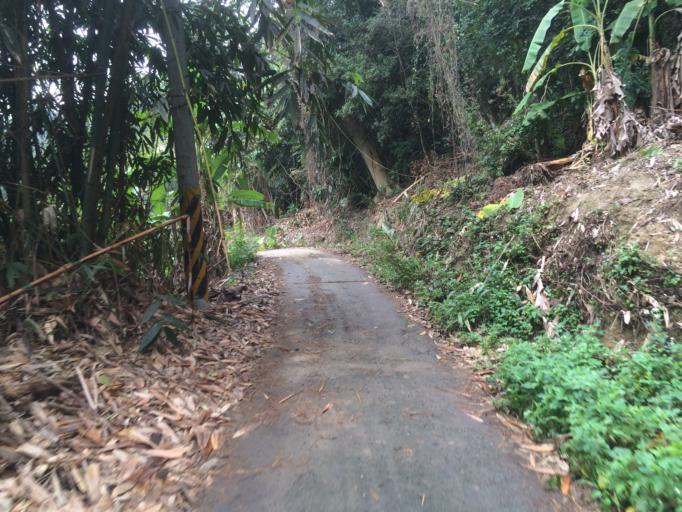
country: TW
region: Taiwan
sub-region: Taichung City
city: Taichung
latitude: 24.1634
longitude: 120.7799
